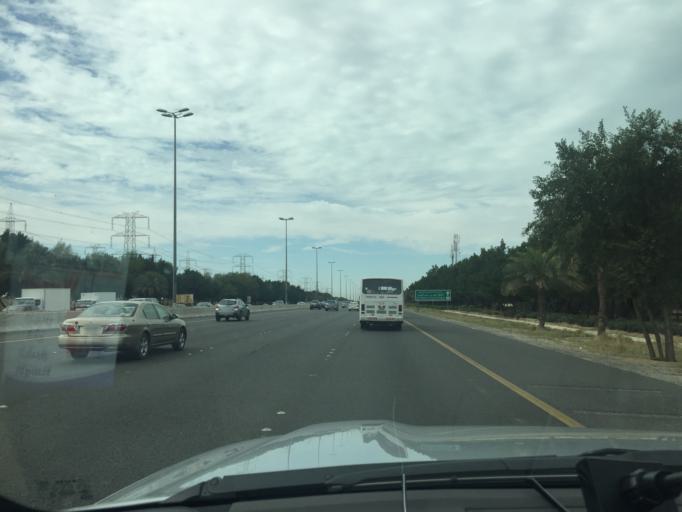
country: KW
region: Mubarak al Kabir
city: Sabah as Salim
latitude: 29.2455
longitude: 48.0483
